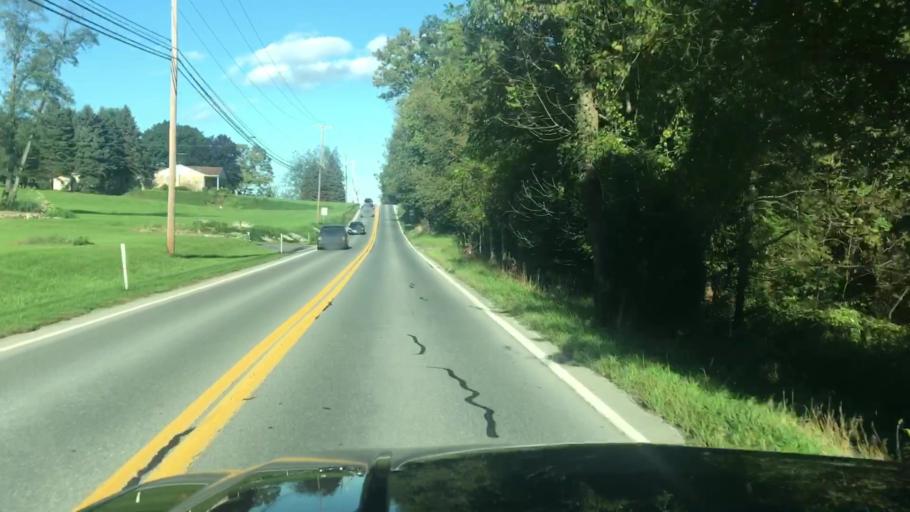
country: US
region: Pennsylvania
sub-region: Cumberland County
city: Shiremanstown
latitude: 40.1724
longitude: -76.9621
